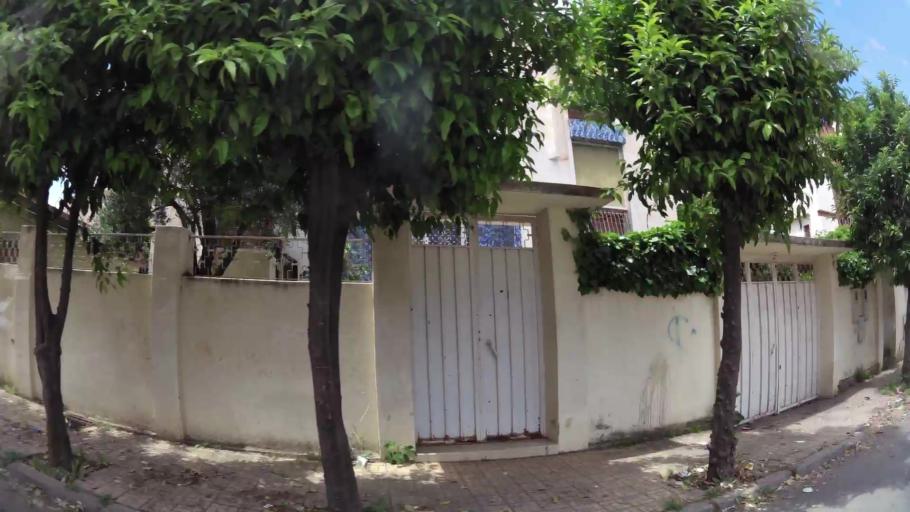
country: MA
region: Fes-Boulemane
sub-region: Fes
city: Fes
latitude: 34.0364
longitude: -5.0210
